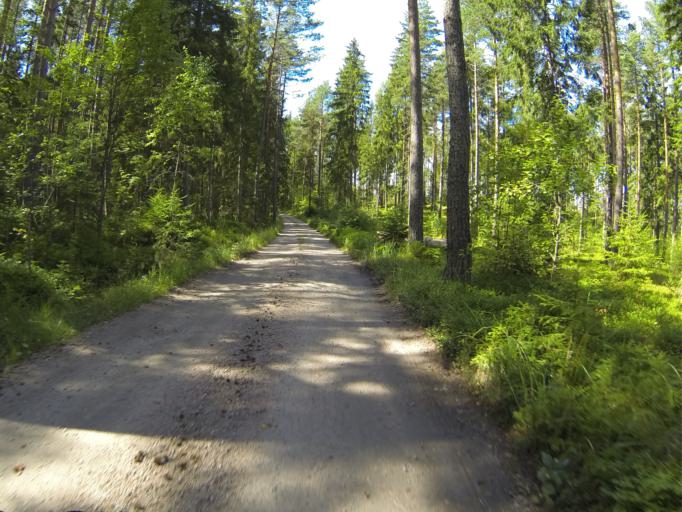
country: FI
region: Varsinais-Suomi
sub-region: Salo
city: Pernioe
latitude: 60.2798
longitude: 23.0305
